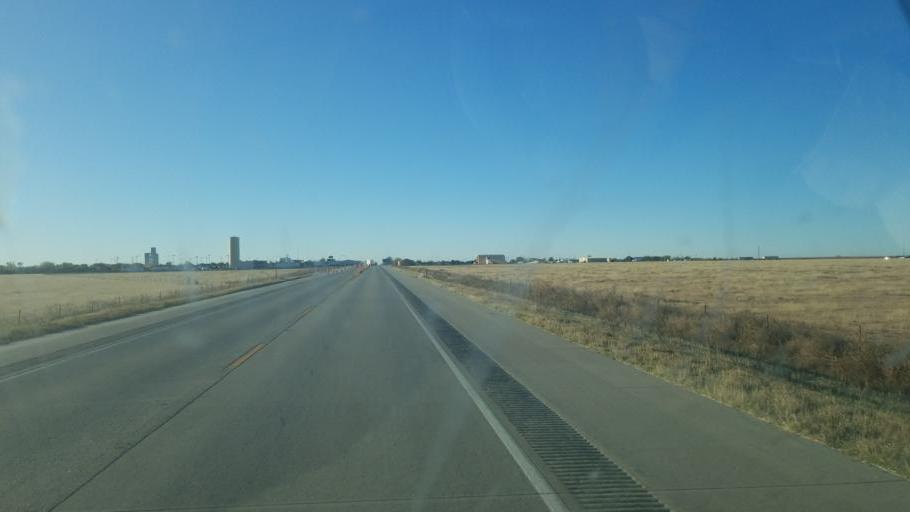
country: US
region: Colorado
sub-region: Kiowa County
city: Eads
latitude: 38.4937
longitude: -102.7857
